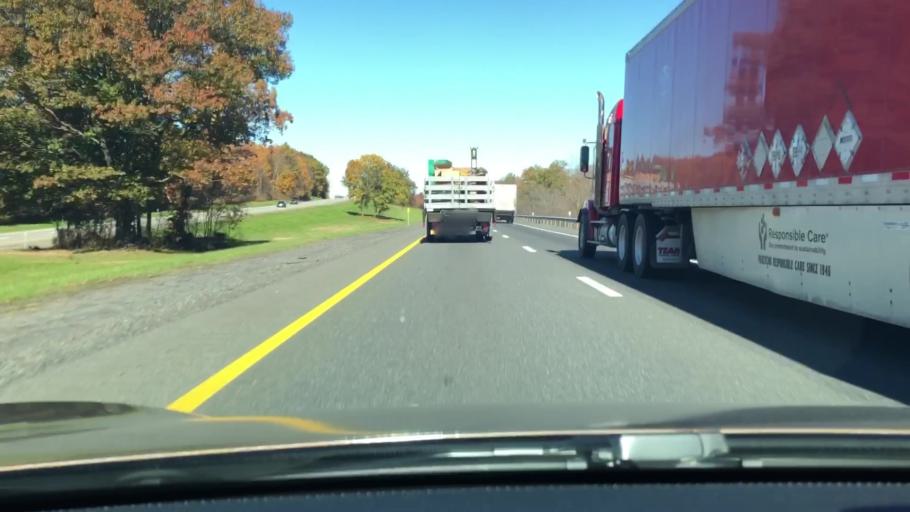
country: US
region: New York
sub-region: Ulster County
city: Plattekill
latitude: 41.6024
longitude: -74.0840
